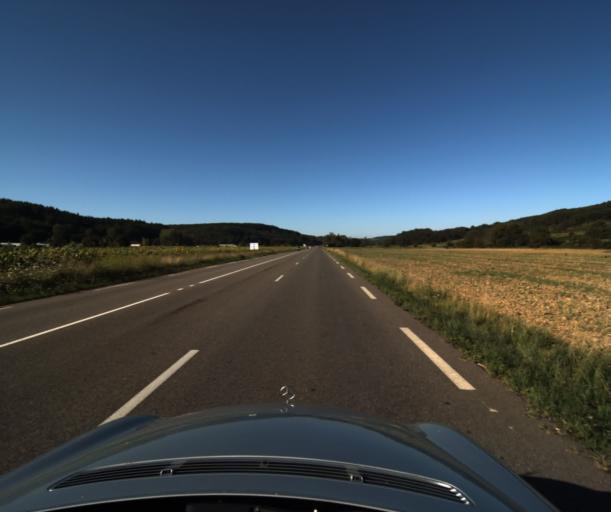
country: FR
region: Midi-Pyrenees
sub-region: Departement de l'Ariege
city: Lavelanet
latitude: 43.0002
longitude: 1.8811
